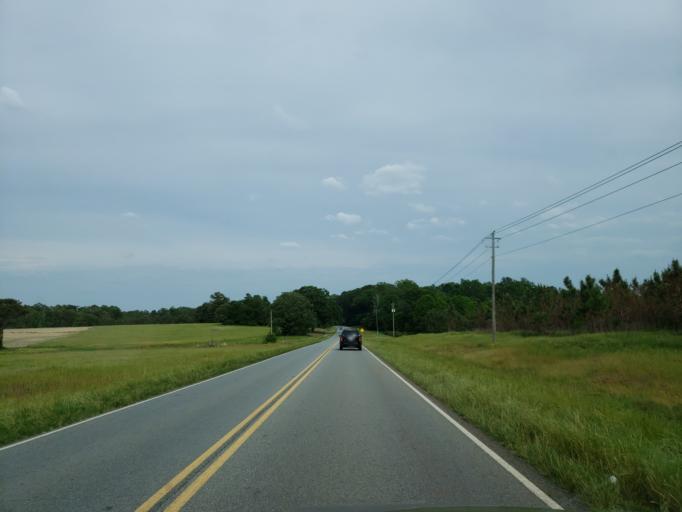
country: US
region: Georgia
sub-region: Dooly County
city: Vienna
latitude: 32.1115
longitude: -83.8456
